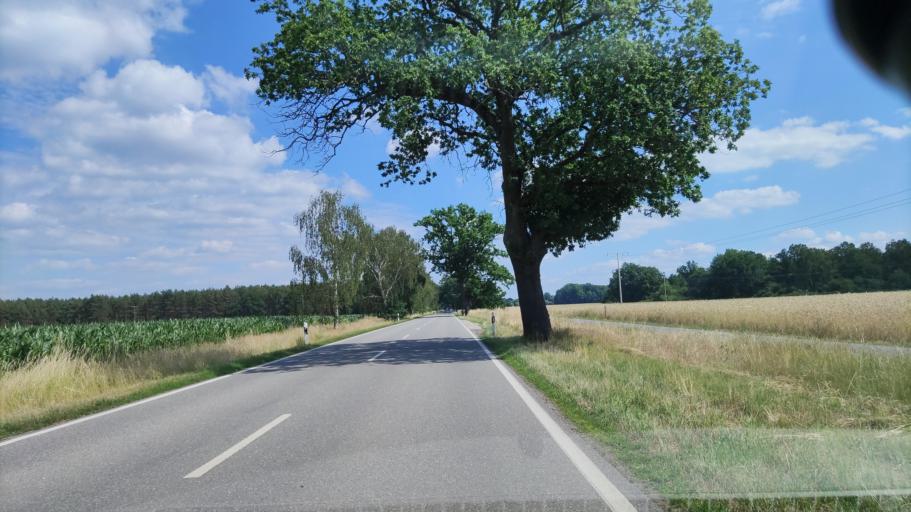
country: DE
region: Mecklenburg-Vorpommern
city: Lubtheen
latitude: 53.2684
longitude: 11.0913
